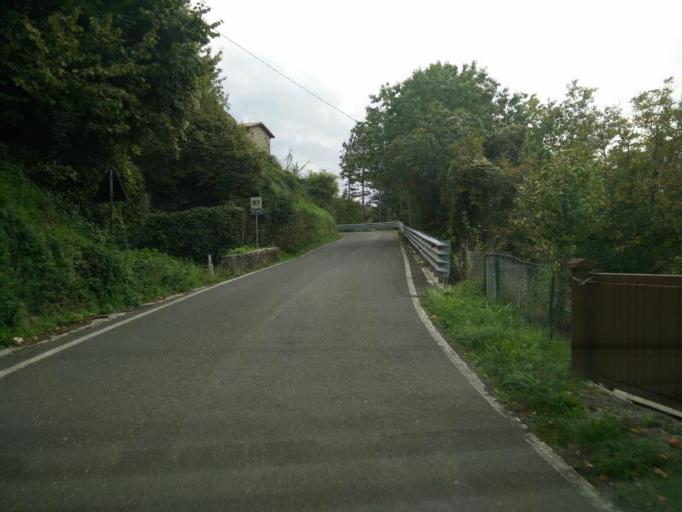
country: IT
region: Tuscany
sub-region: Provincia di Massa-Carrara
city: Casola in Lunigiana
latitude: 44.2186
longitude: 10.1976
